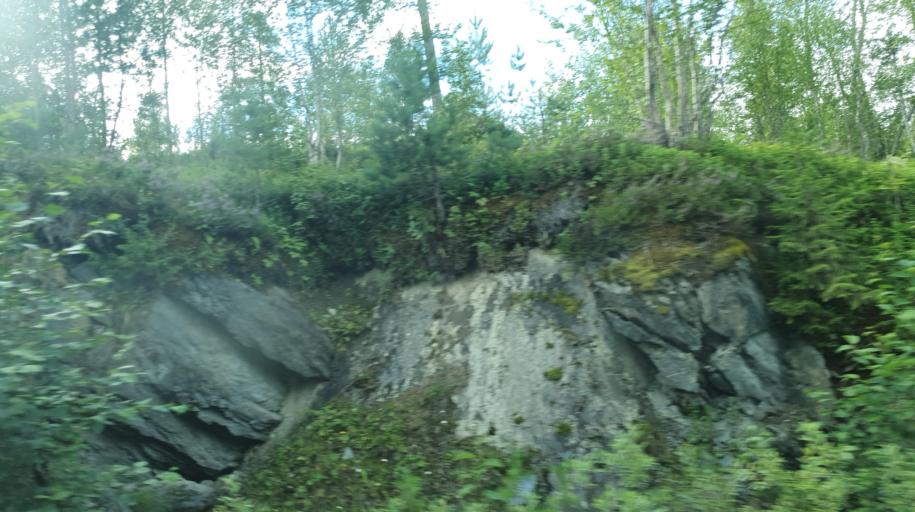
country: NO
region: Nord-Trondelag
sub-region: Levanger
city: Skogn
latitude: 63.5838
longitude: 11.2444
